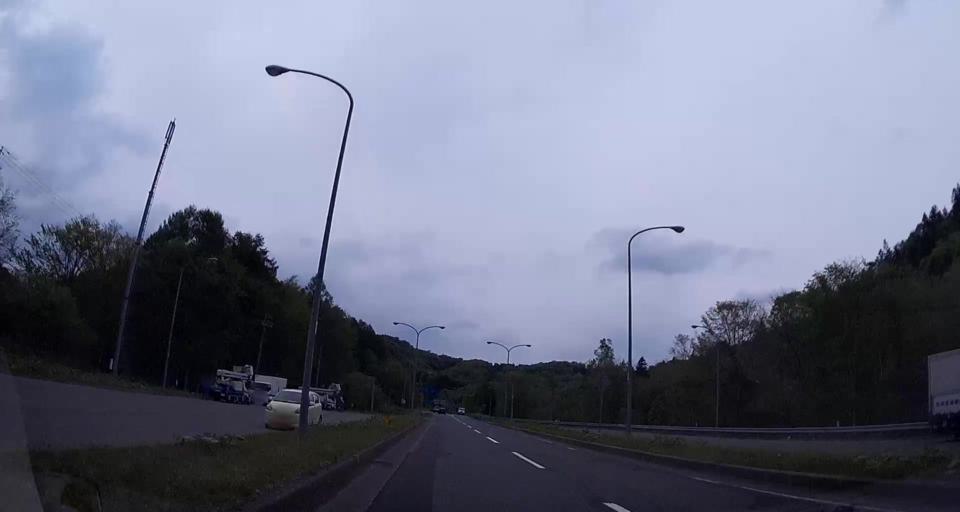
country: JP
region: Hokkaido
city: Shiraoi
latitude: 42.6936
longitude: 141.1063
